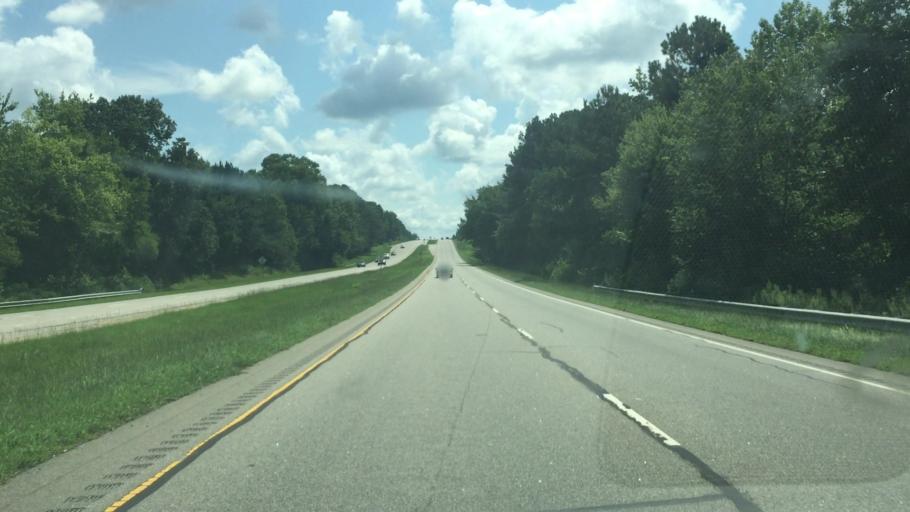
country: US
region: North Carolina
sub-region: Anson County
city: Wadesboro
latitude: 34.9636
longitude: -80.0210
